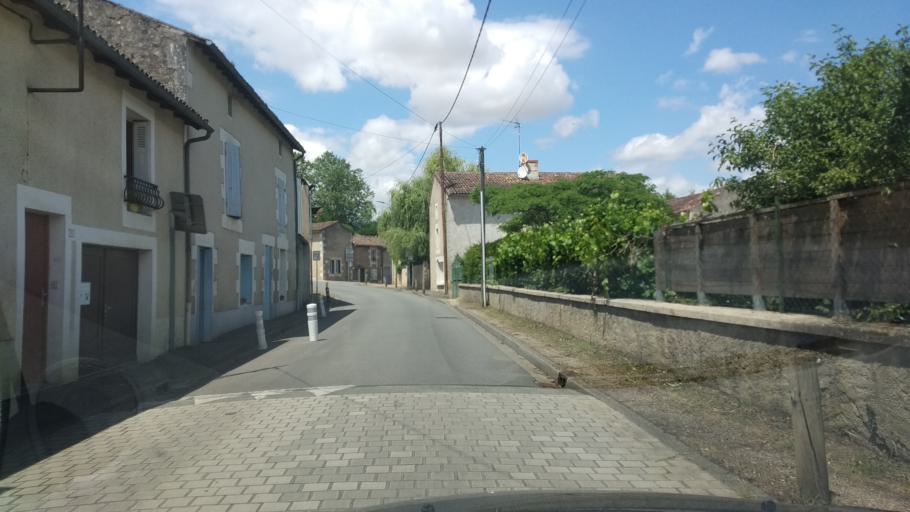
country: FR
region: Poitou-Charentes
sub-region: Departement de la Vienne
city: Cisse
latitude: 46.6058
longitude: 0.2386
